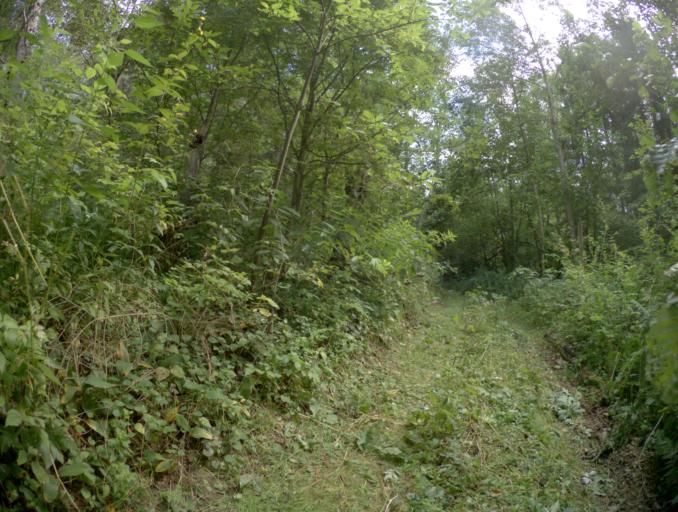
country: RU
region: Vladimir
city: Orgtrud
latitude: 56.0797
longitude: 40.5864
